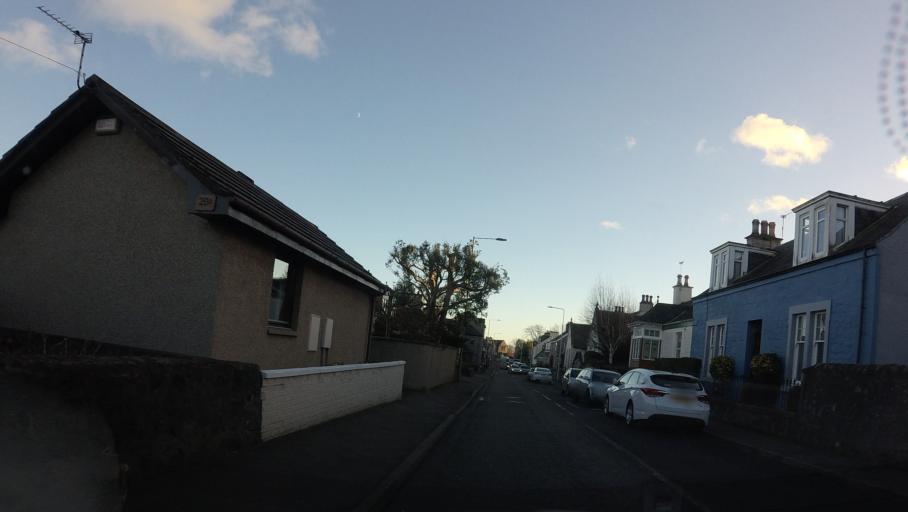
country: GB
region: Scotland
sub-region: Fife
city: Tayport
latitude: 56.4490
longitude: -2.8817
